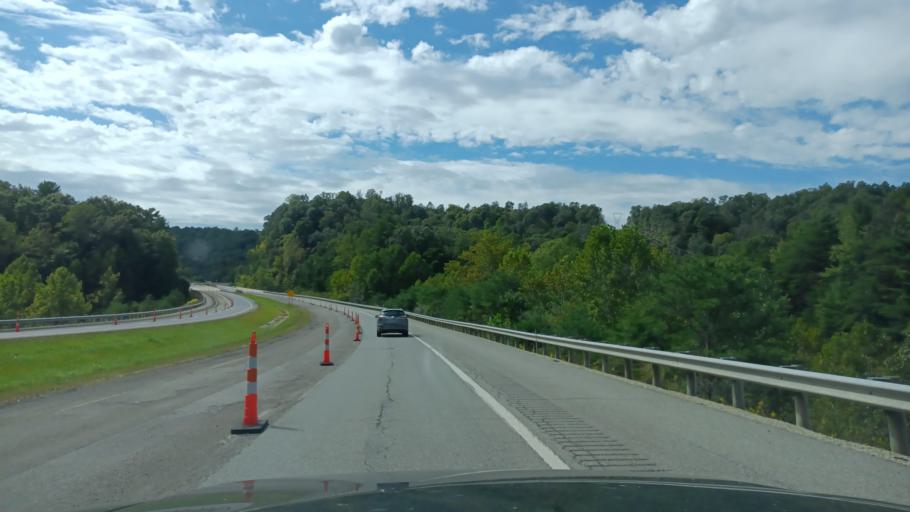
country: US
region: West Virginia
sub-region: Ritchie County
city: Harrisville
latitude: 39.2609
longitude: -81.1022
